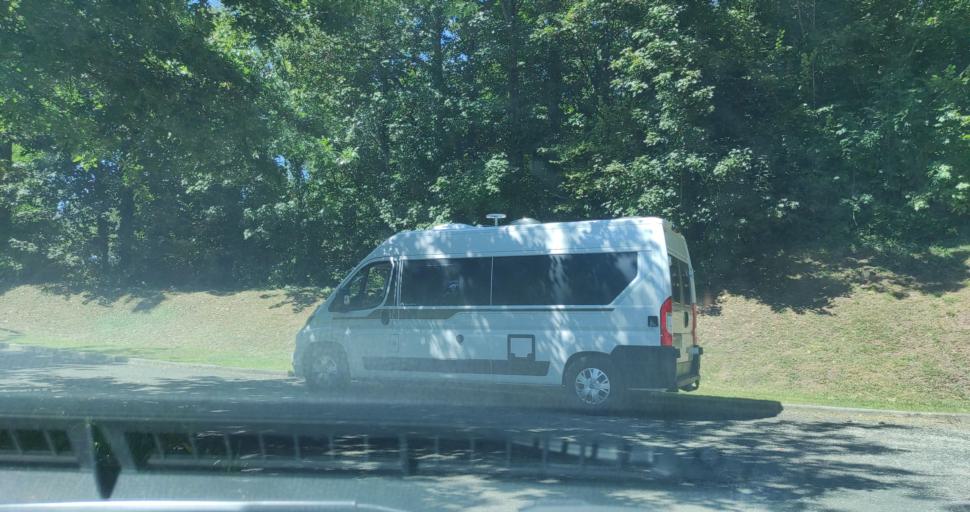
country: FR
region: Midi-Pyrenees
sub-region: Departement de l'Aveyron
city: Cransac
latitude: 44.5284
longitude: 2.2753
